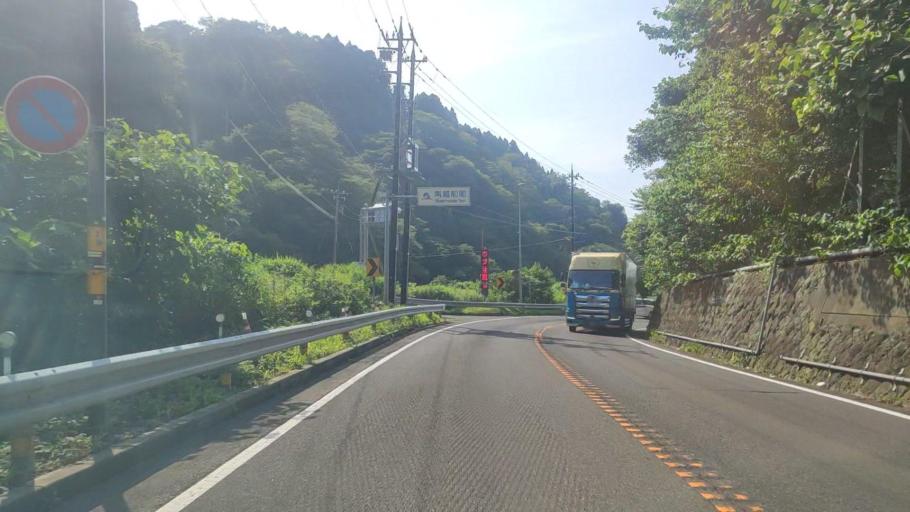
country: JP
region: Fukui
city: Tsuruga
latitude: 35.7715
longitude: 136.1063
